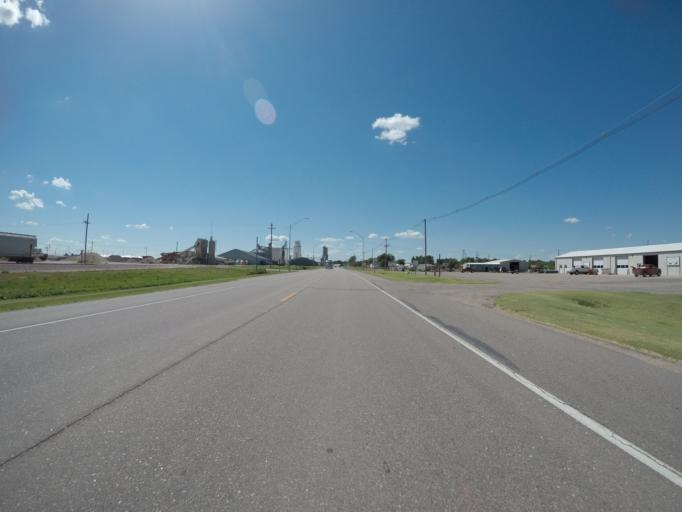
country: US
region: Nebraska
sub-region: Chase County
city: Imperial
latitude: 40.5105
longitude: -101.6370
